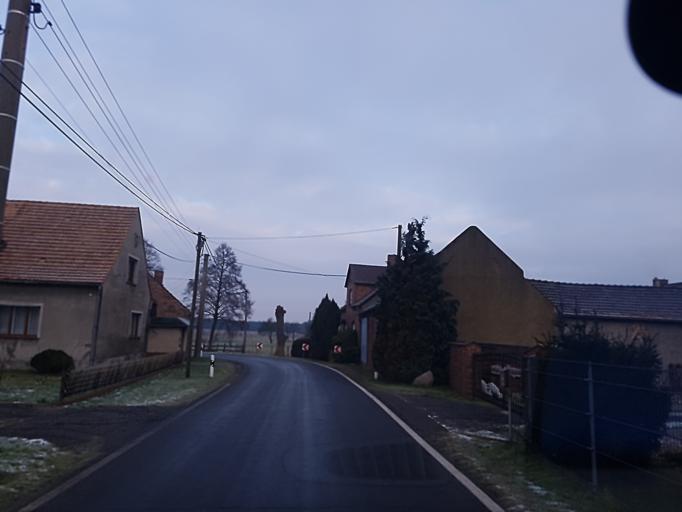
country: DE
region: Brandenburg
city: Crinitz
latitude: 51.7340
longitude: 13.8321
